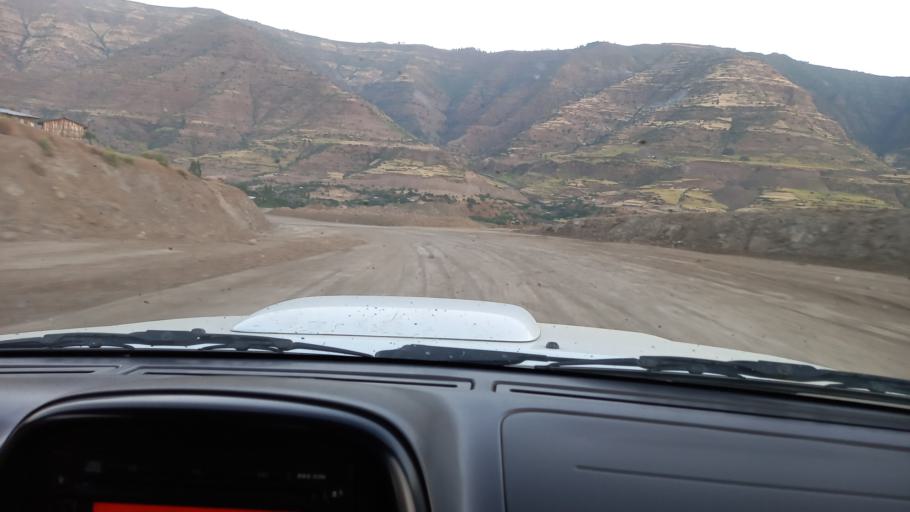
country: ET
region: Amhara
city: Debark'
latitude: 13.0360
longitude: 38.0418
